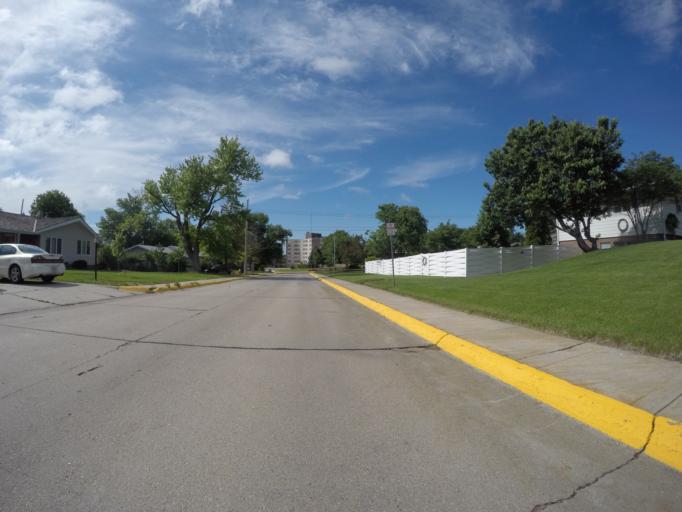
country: US
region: Nebraska
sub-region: Buffalo County
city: Kearney
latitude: 40.7060
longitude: -99.0957
